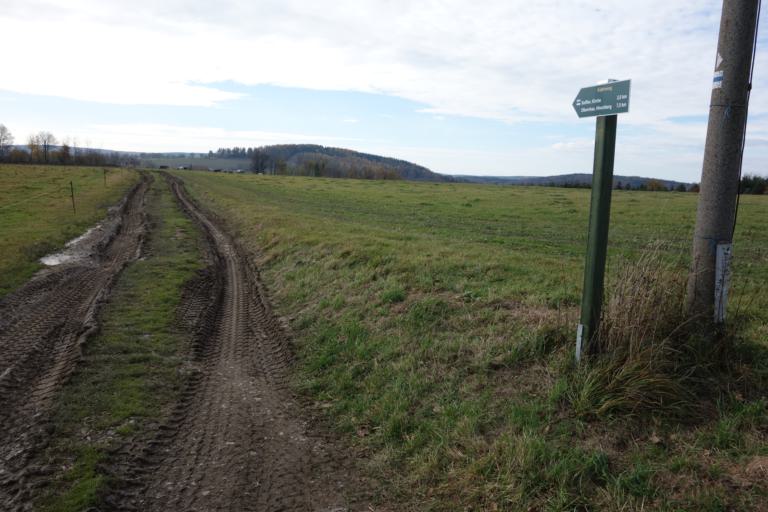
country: DE
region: Saxony
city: Seiffen
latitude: 50.6512
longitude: 13.4617
